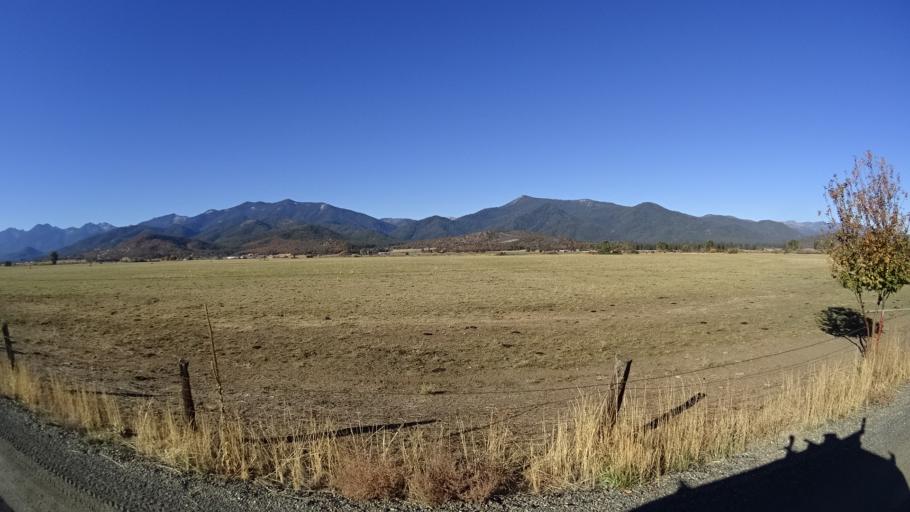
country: US
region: California
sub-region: Siskiyou County
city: Yreka
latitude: 41.4497
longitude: -122.8468
